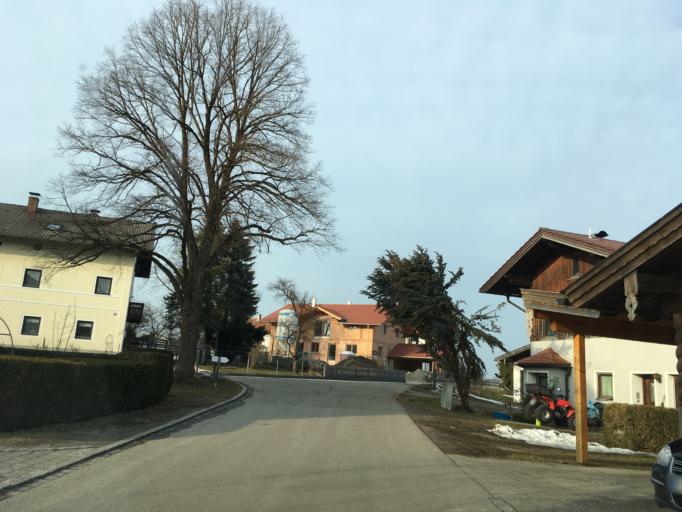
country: DE
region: Bavaria
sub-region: Upper Bavaria
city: Sochtenau
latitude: 47.9318
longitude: 12.2317
